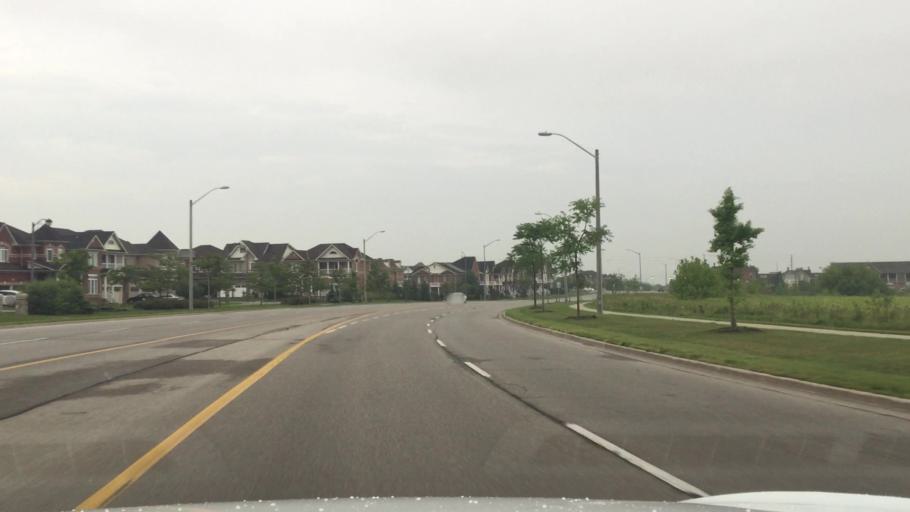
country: CA
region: Ontario
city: Markham
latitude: 43.8639
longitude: -79.2261
